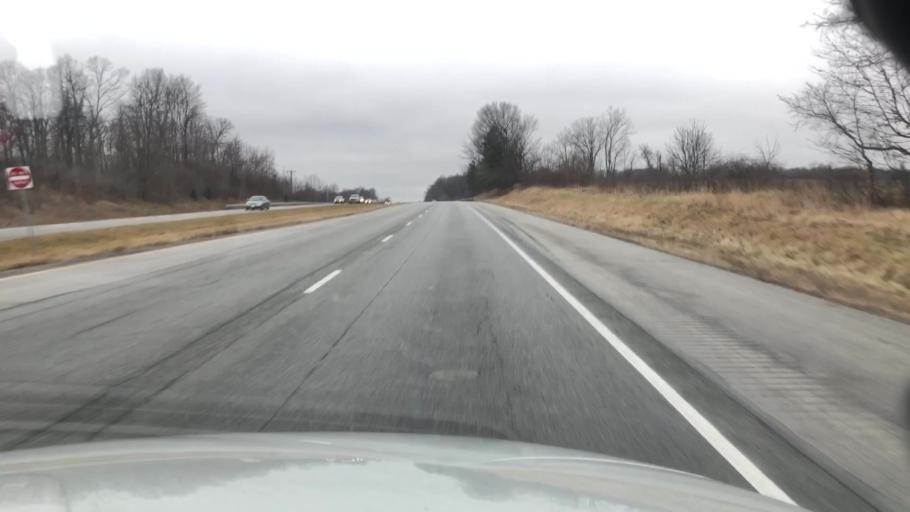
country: US
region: Indiana
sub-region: Whitley County
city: Columbia City
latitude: 41.1776
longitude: -85.5776
